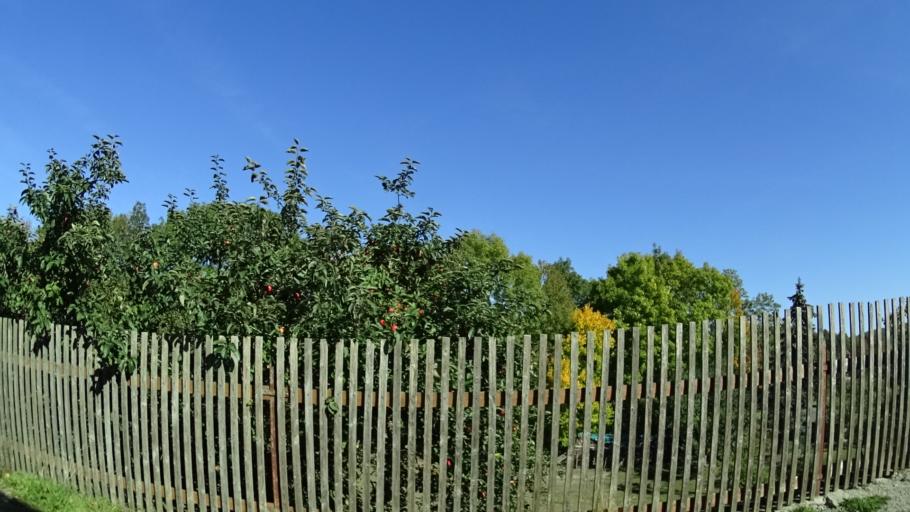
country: DE
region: Thuringia
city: Rittersdorf
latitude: 50.7592
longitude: 11.2298
